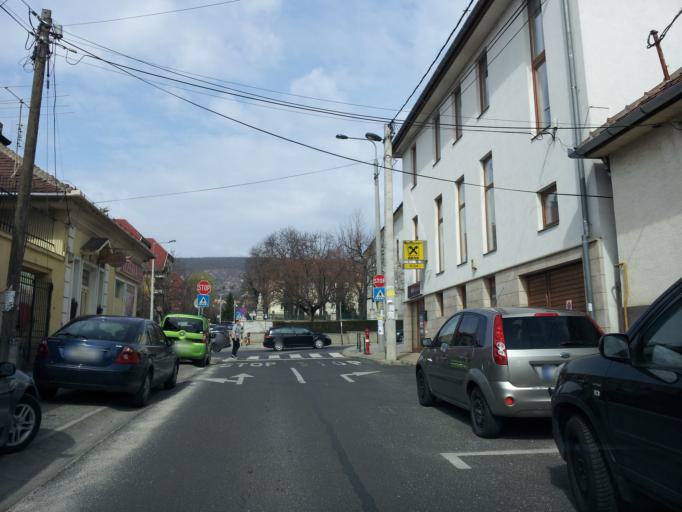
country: HU
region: Pest
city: Budaors
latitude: 47.4609
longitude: 18.9627
